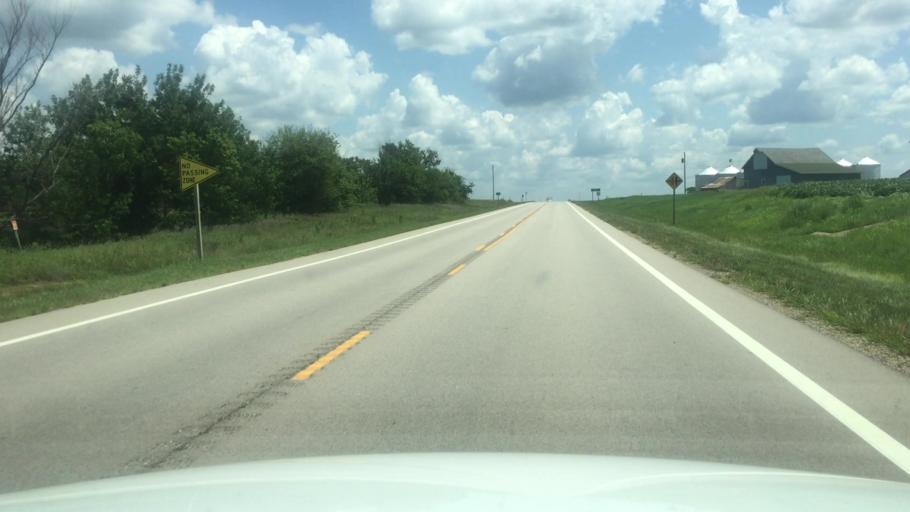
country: US
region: Kansas
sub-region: Brown County
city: Horton
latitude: 39.6536
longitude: -95.3655
